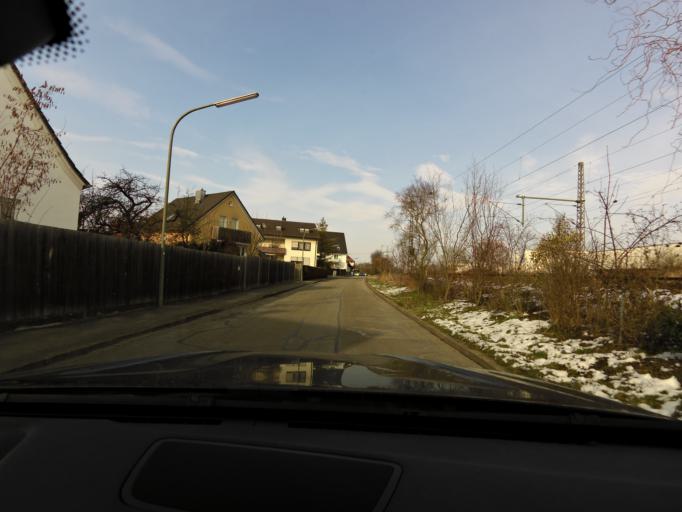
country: DE
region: Bavaria
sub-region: Lower Bavaria
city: Ergolding
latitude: 48.5581
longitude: 12.1446
